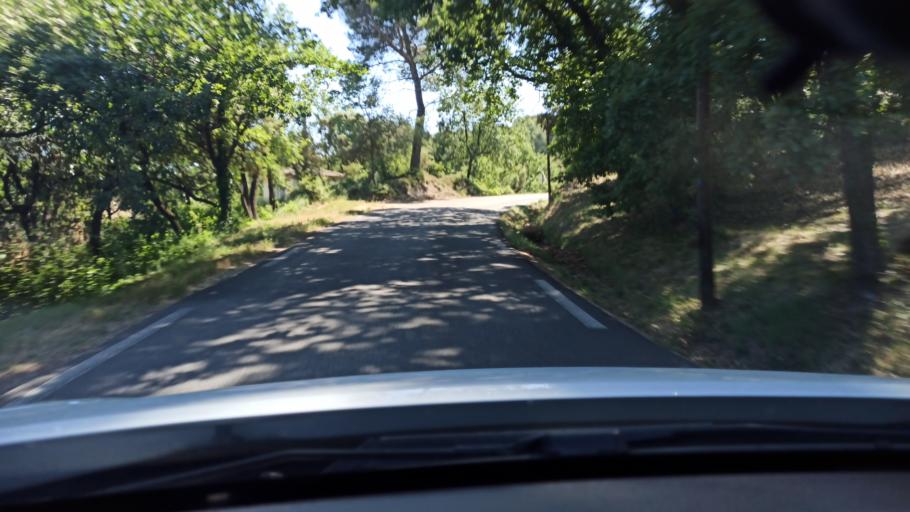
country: FR
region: Provence-Alpes-Cote d'Azur
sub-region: Departement des Bouches-du-Rhone
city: Noves
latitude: 43.8663
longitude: 4.8833
